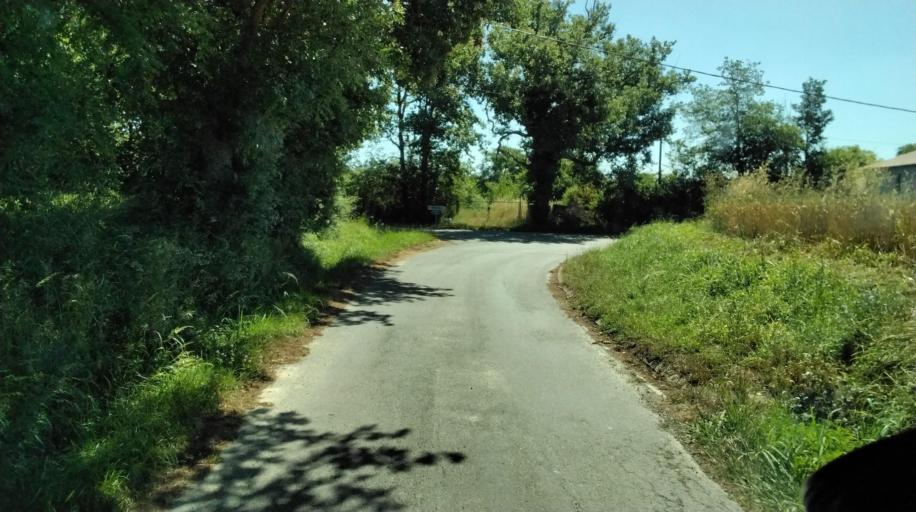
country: FR
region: Midi-Pyrenees
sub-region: Departement de la Haute-Garonne
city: Sainte-Foy-de-Peyrolieres
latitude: 43.4847
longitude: 1.1518
